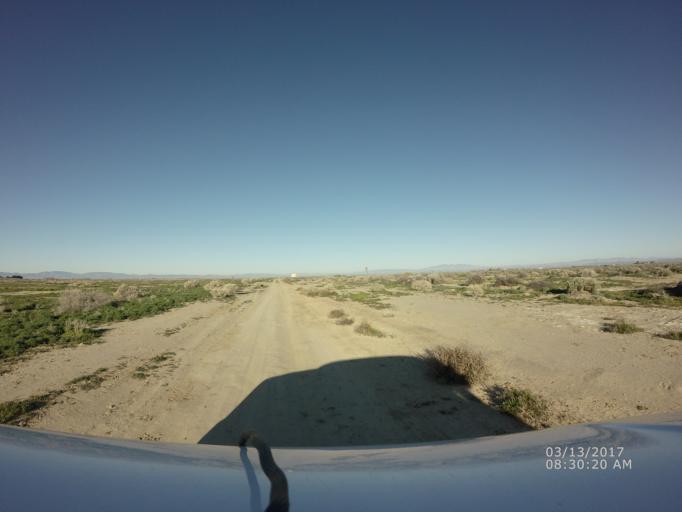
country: US
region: California
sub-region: Los Angeles County
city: Lake Los Angeles
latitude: 34.7342
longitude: -117.9446
